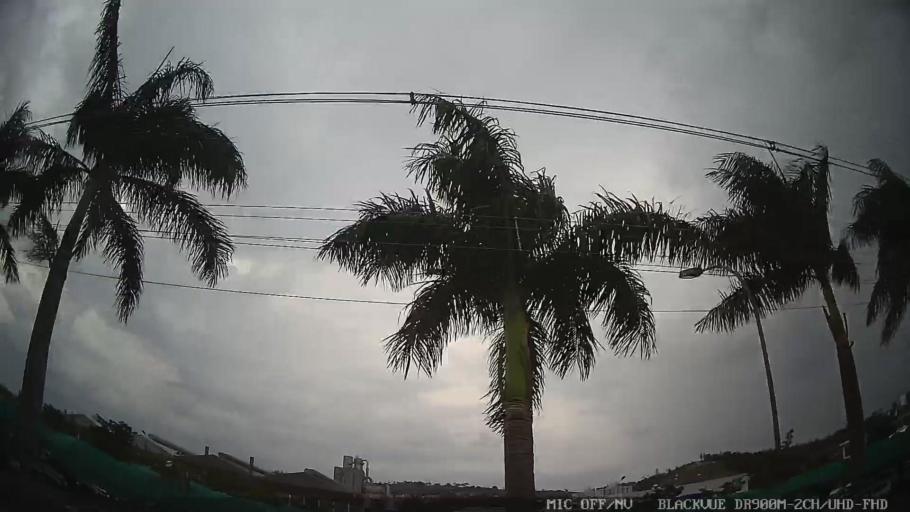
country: BR
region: Sao Paulo
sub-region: Amparo
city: Amparo
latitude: -22.7198
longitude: -46.7866
